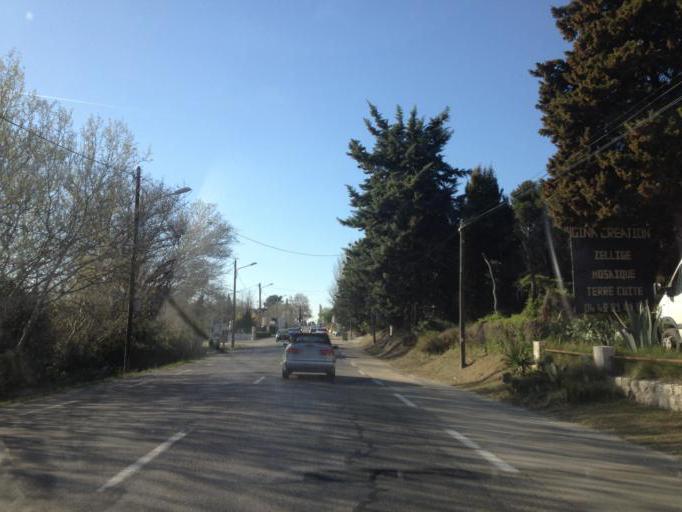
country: FR
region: Provence-Alpes-Cote d'Azur
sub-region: Departement des Bouches-du-Rhone
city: Aix-en-Provence
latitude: 43.5532
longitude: 5.4231
